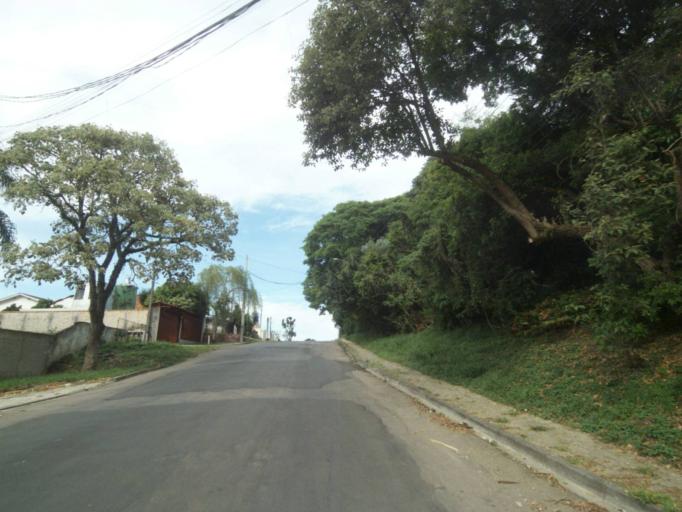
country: BR
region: Parana
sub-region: Pinhais
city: Pinhais
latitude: -25.4197
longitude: -49.2125
